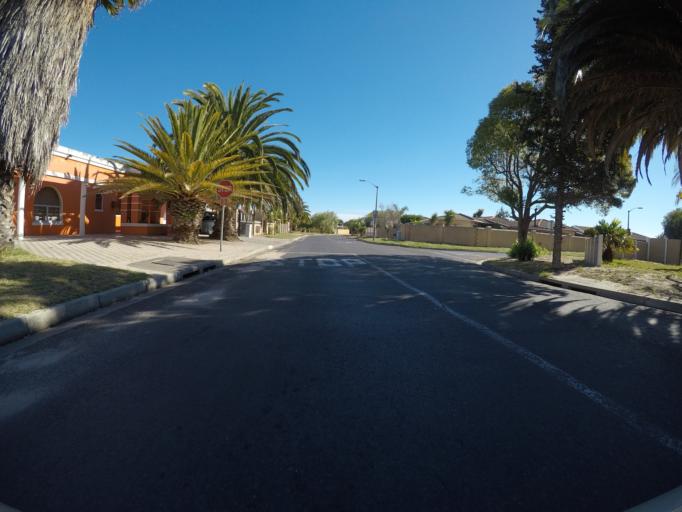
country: ZA
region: Western Cape
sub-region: City of Cape Town
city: Kraaifontein
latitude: -33.9439
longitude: 18.6834
